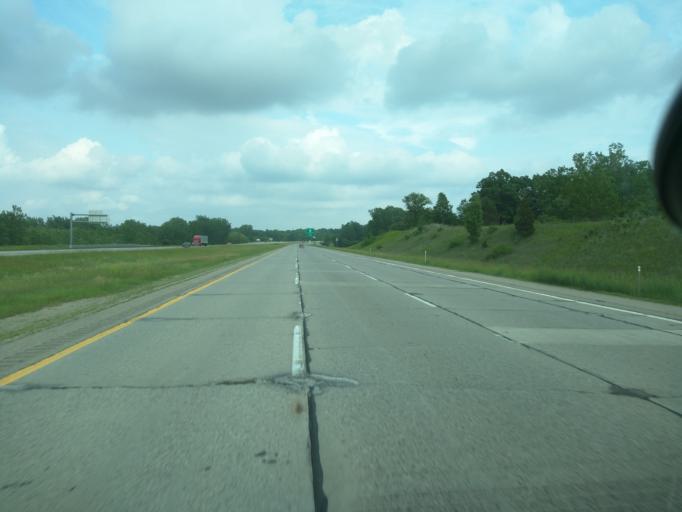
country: US
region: Michigan
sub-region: Clinton County
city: DeWitt
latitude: 42.8175
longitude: -84.5350
